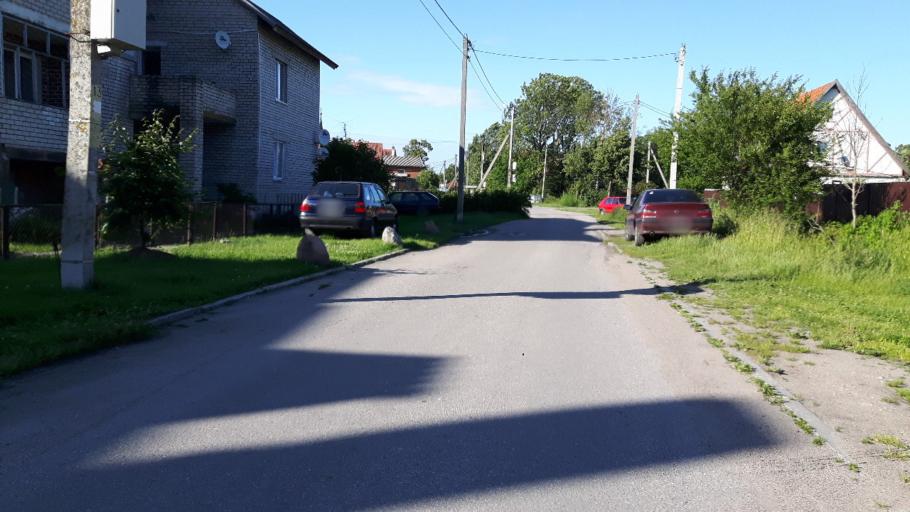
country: LT
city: Nida
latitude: 55.1514
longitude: 20.8542
